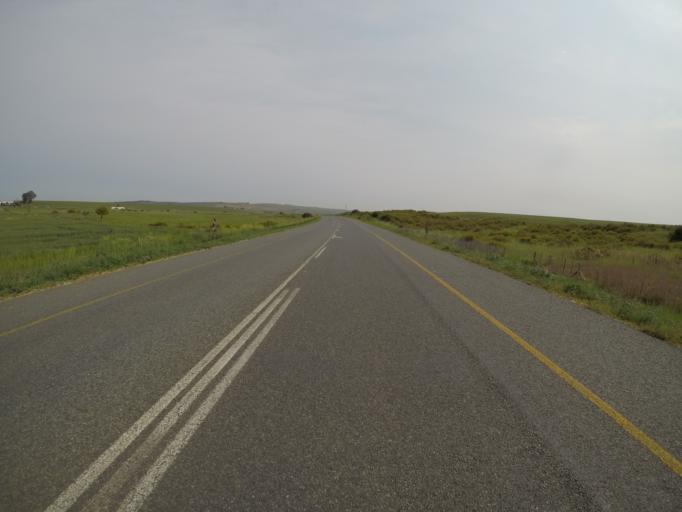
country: ZA
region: Western Cape
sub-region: West Coast District Municipality
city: Malmesbury
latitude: -33.4531
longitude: 18.7792
